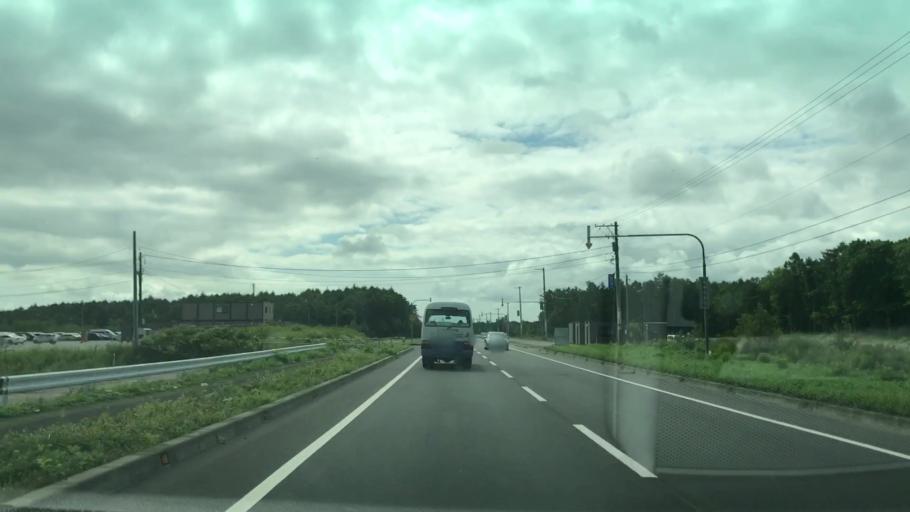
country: JP
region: Hokkaido
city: Chitose
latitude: 42.7709
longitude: 141.6793
